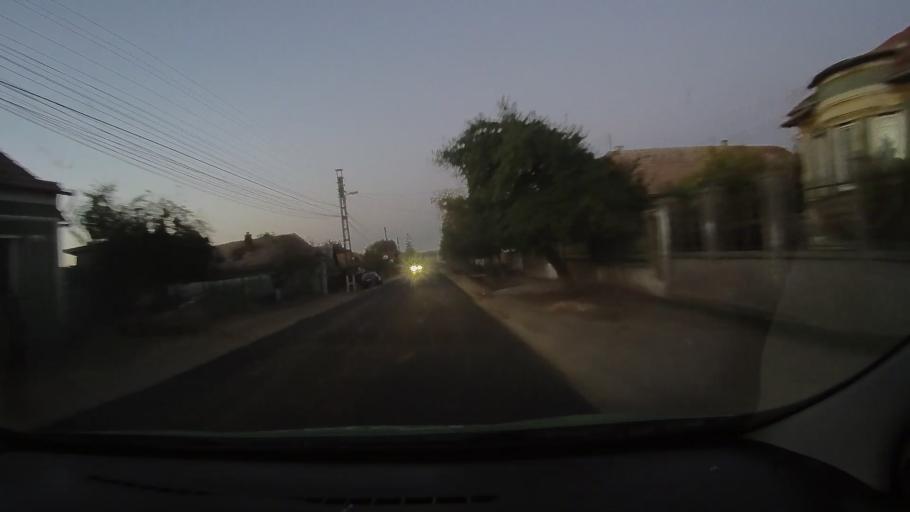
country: RO
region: Bihor
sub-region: Comuna Simian
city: Simian
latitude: 47.5016
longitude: 22.0915
